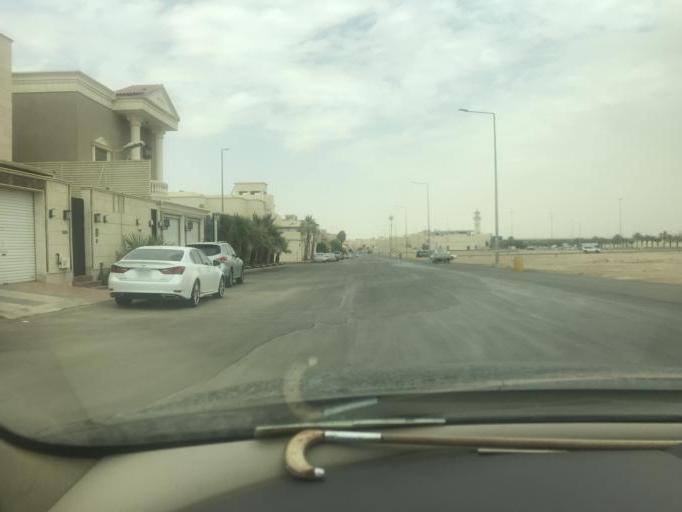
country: SA
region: Ar Riyad
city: Riyadh
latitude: 24.7902
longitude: 46.7127
